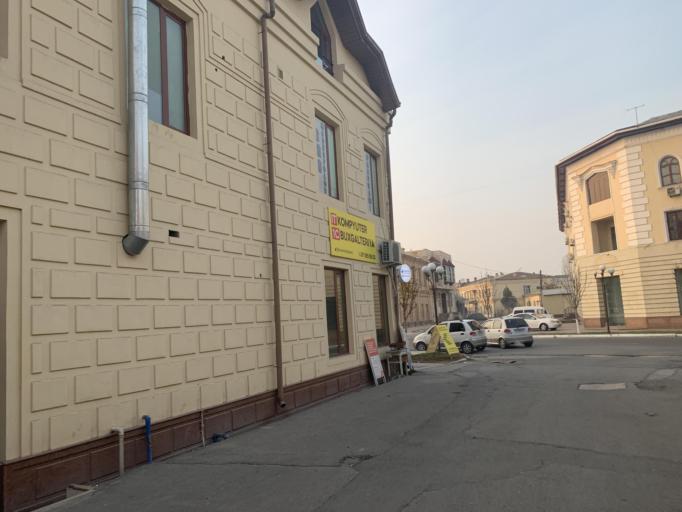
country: UZ
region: Fergana
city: Qo`qon
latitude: 40.5365
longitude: 70.9329
